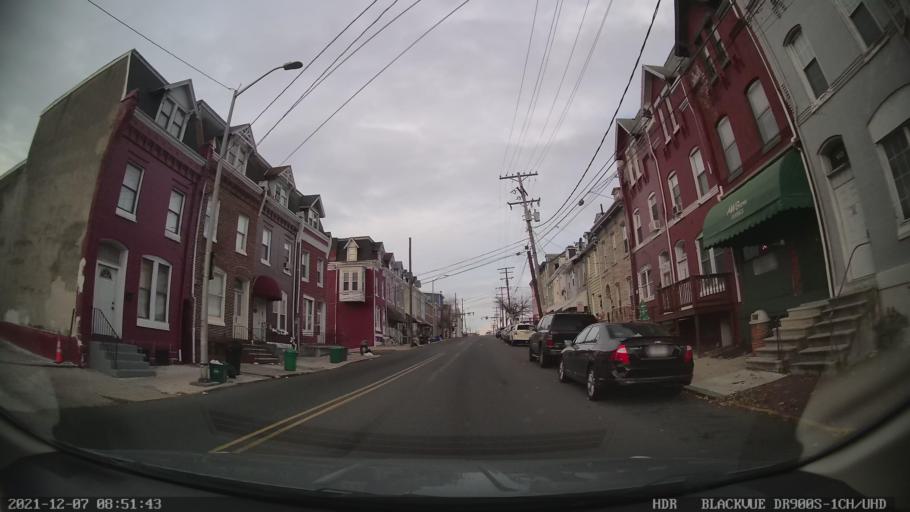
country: US
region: Pennsylvania
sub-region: Berks County
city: Reading
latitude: 40.3416
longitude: -75.9283
